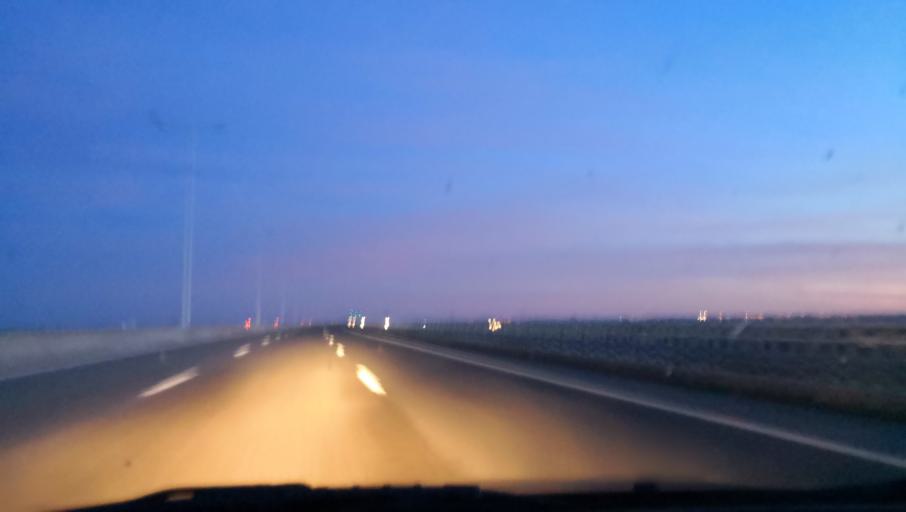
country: PT
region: Lisbon
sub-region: Vila Franca de Xira
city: Castanheira do Ribatejo
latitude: 39.0004
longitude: -8.9050
